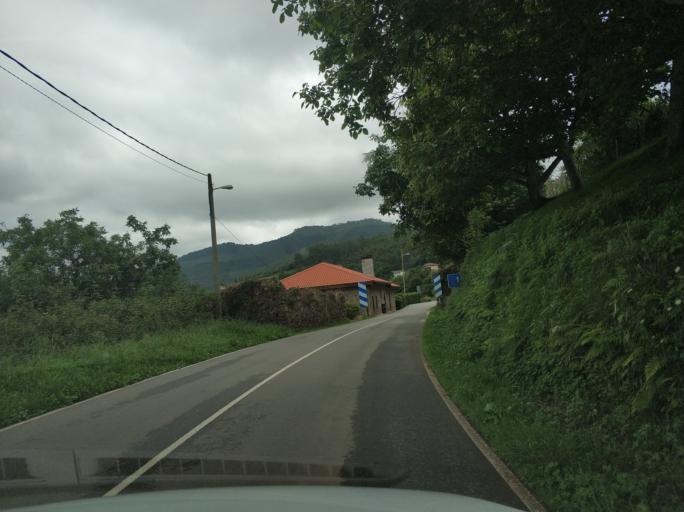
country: ES
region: Asturias
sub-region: Province of Asturias
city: Cudillero
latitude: 43.5424
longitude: -6.2344
